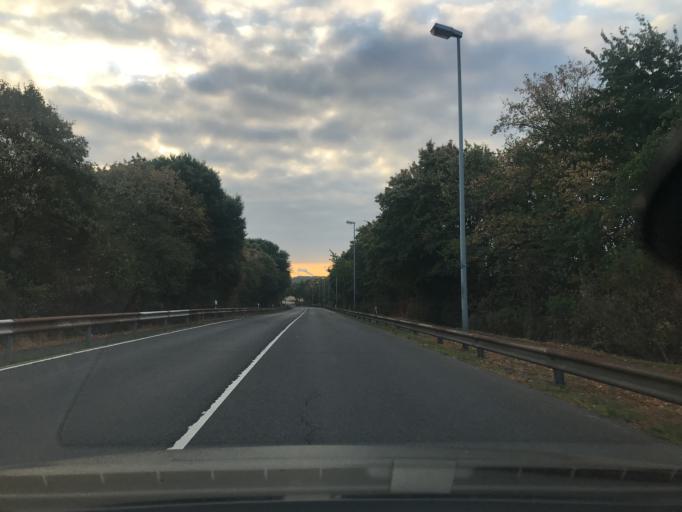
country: DE
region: North Rhine-Westphalia
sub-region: Regierungsbezirk Dusseldorf
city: Krefeld
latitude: 51.3757
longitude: 6.6234
